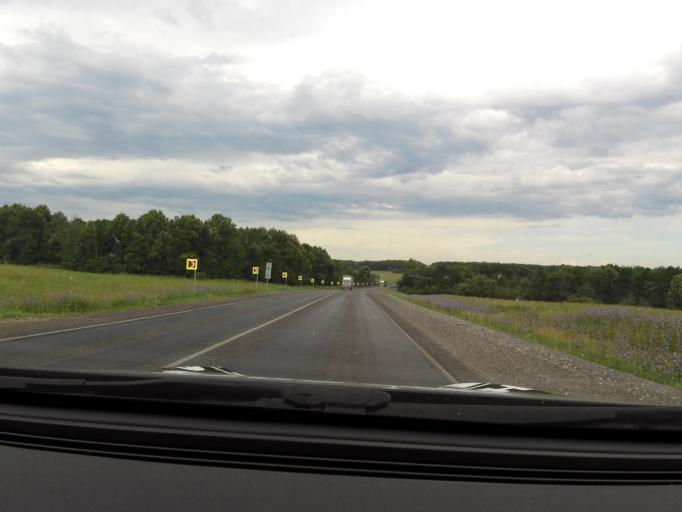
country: RU
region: Bashkortostan
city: Urman
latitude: 54.8179
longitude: 56.8701
